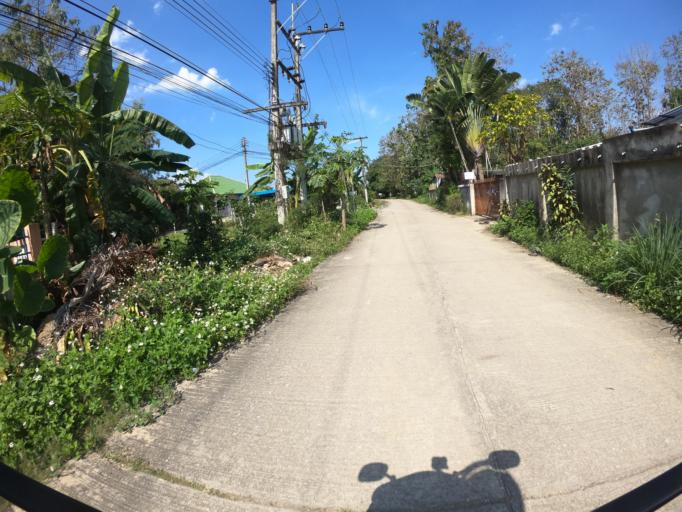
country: TH
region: Chiang Mai
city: San Sai
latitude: 18.8712
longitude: 98.9764
